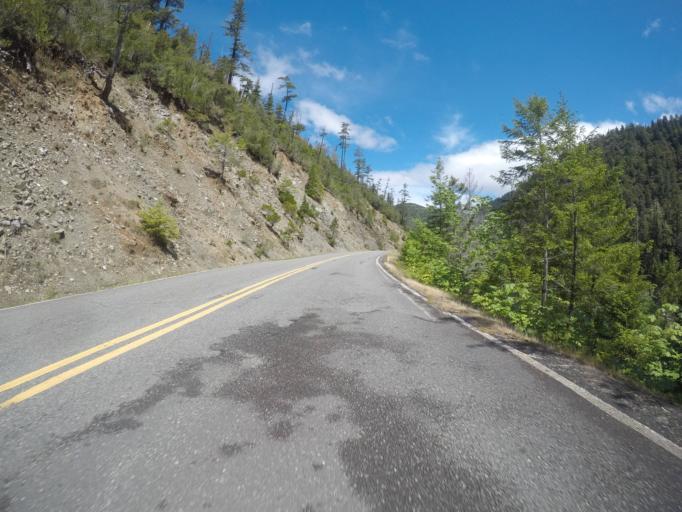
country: US
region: California
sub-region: Del Norte County
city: Bertsch-Oceanview
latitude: 41.7067
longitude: -123.9406
